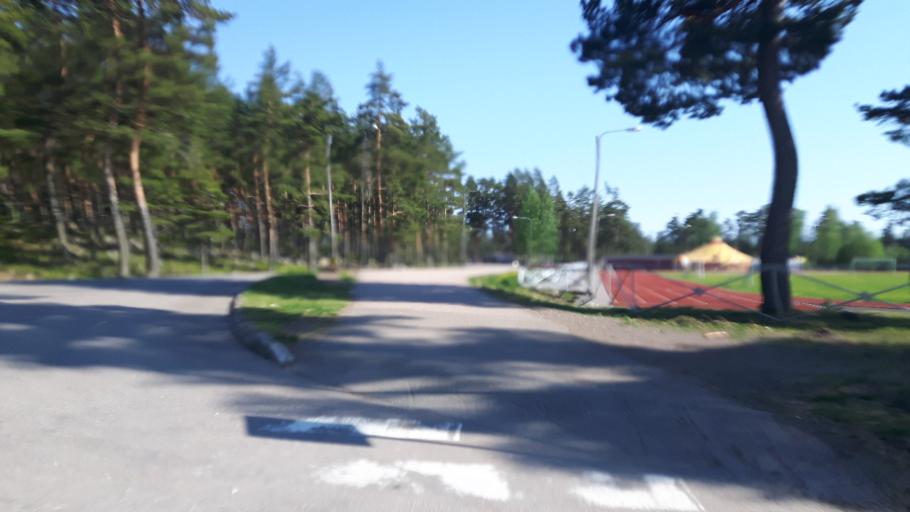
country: FI
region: Kymenlaakso
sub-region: Kotka-Hamina
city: Broby
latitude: 60.4887
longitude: 26.7470
